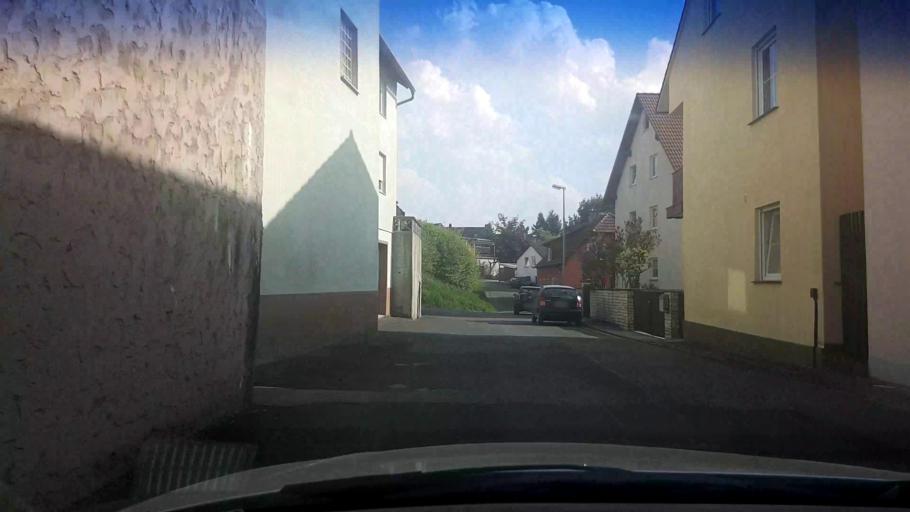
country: DE
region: Bavaria
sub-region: Upper Franconia
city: Rattelsdorf
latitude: 50.0148
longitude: 10.8839
